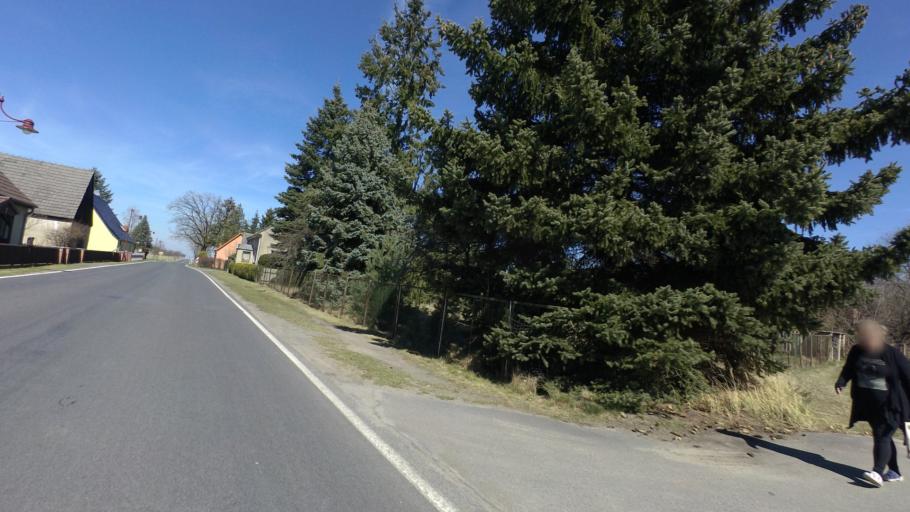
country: DE
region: Brandenburg
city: Munchehofe
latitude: 52.1631
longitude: 13.9208
